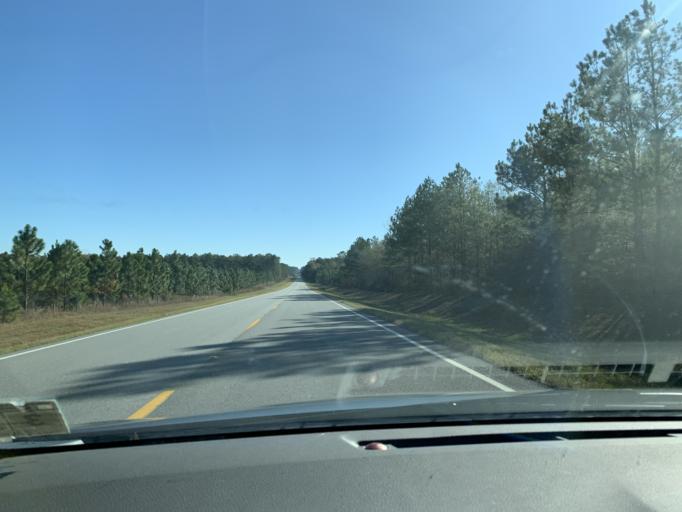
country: US
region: Georgia
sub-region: Ben Hill County
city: Fitzgerald
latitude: 31.7764
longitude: -83.0691
